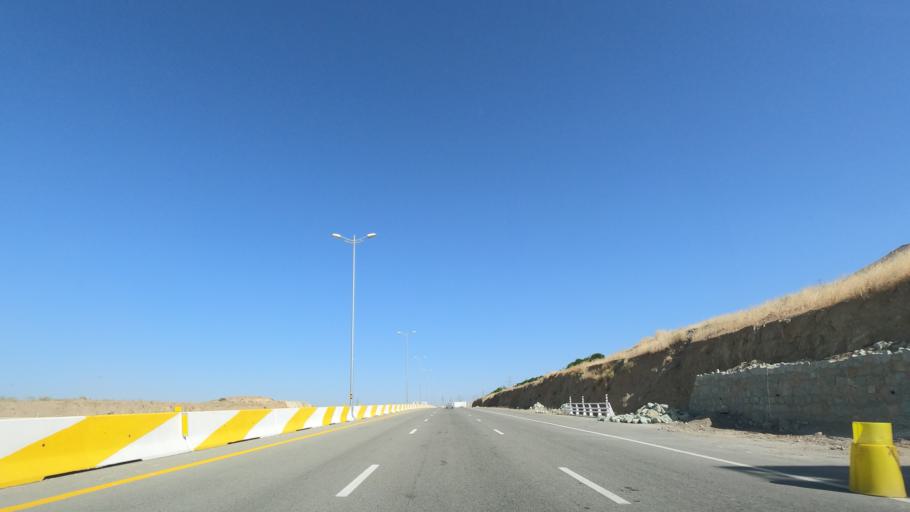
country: IR
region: Tehran
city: Shahr-e Qods
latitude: 35.7663
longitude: 51.0672
